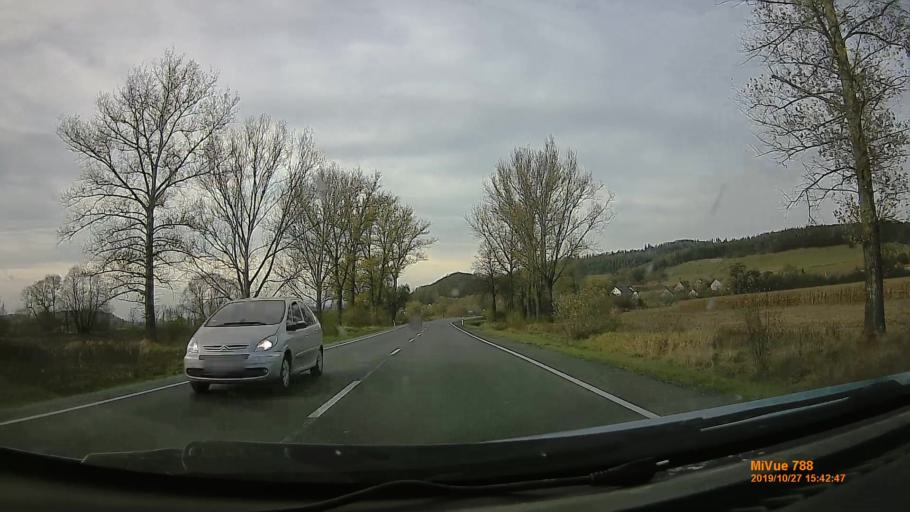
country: PL
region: Lower Silesian Voivodeship
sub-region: Powiat klodzki
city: Klodzko
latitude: 50.4631
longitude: 16.6242
